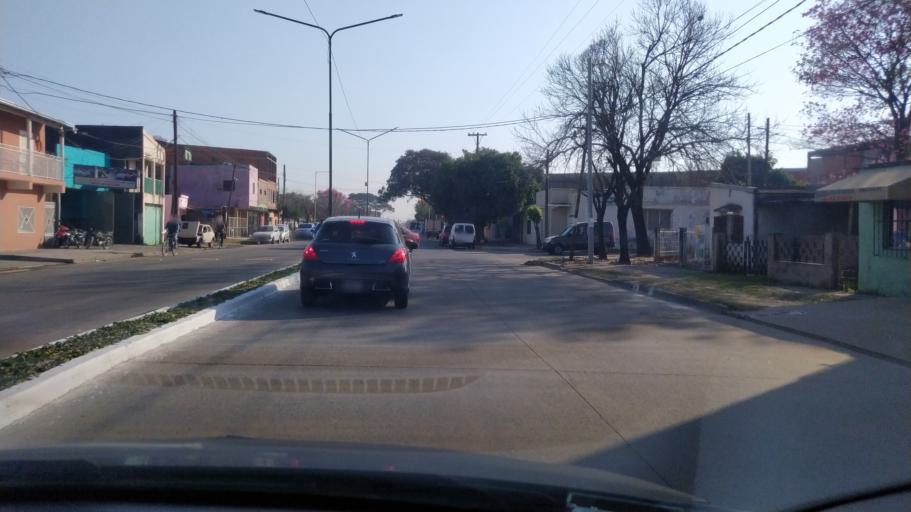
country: AR
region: Corrientes
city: Corrientes
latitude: -27.4905
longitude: -58.8168
